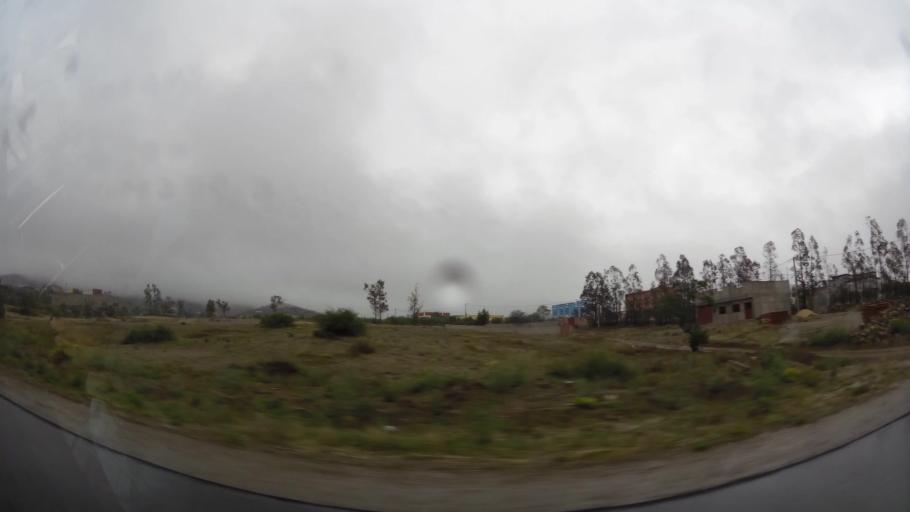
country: MA
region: Taza-Al Hoceima-Taounate
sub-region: Taza
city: Aknoul
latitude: 34.8225
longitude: -3.7246
